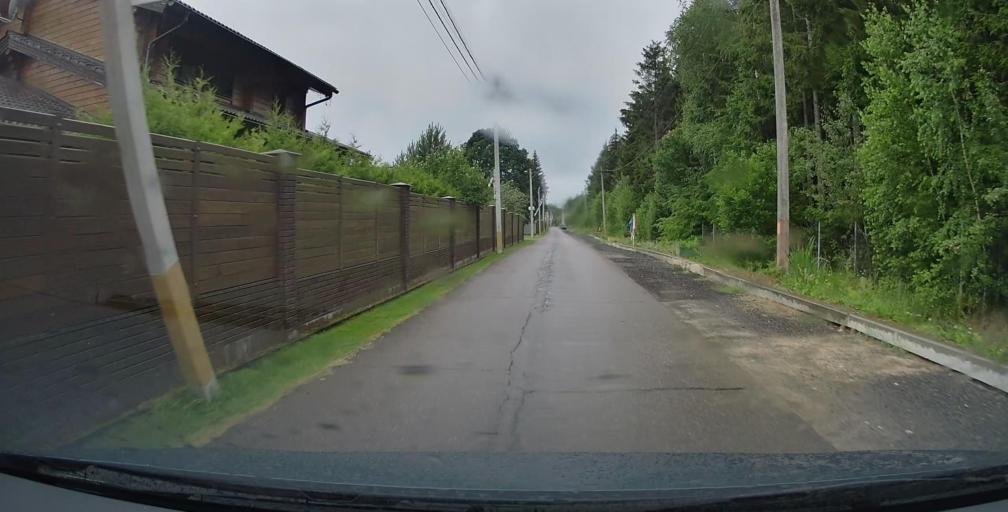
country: RU
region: Moskovskaya
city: Selyatino
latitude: 55.3940
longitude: 37.0151
